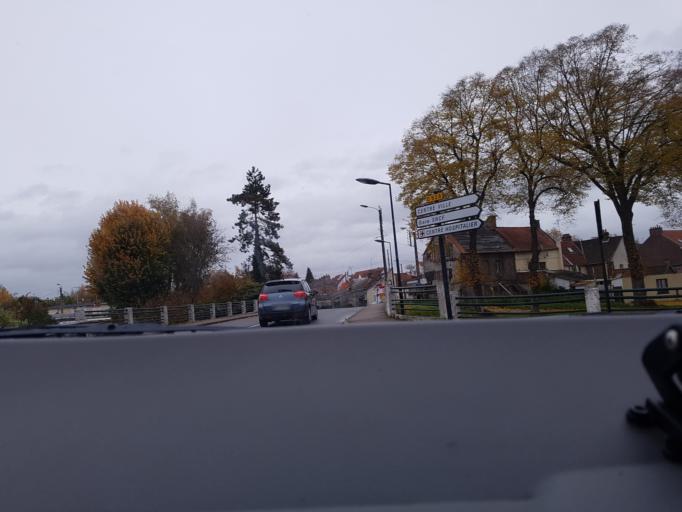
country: FR
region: Picardie
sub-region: Departement de la Somme
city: Abbeville
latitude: 50.1105
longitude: 1.8189
